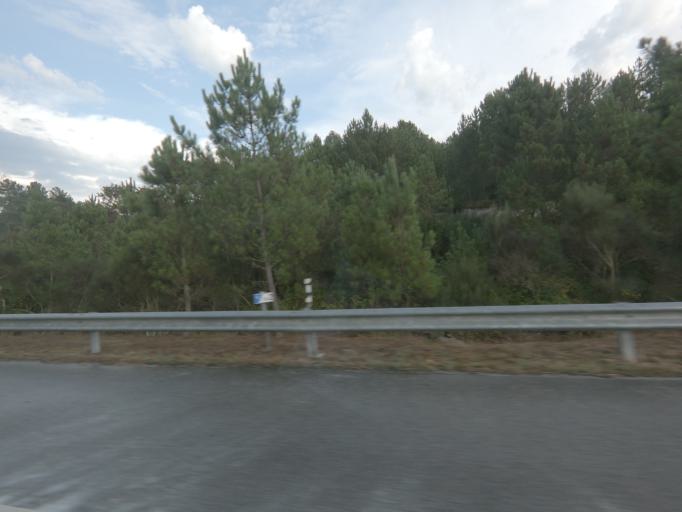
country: PT
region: Viseu
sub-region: Castro Daire
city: Castro Daire
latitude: 40.8717
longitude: -7.9245
